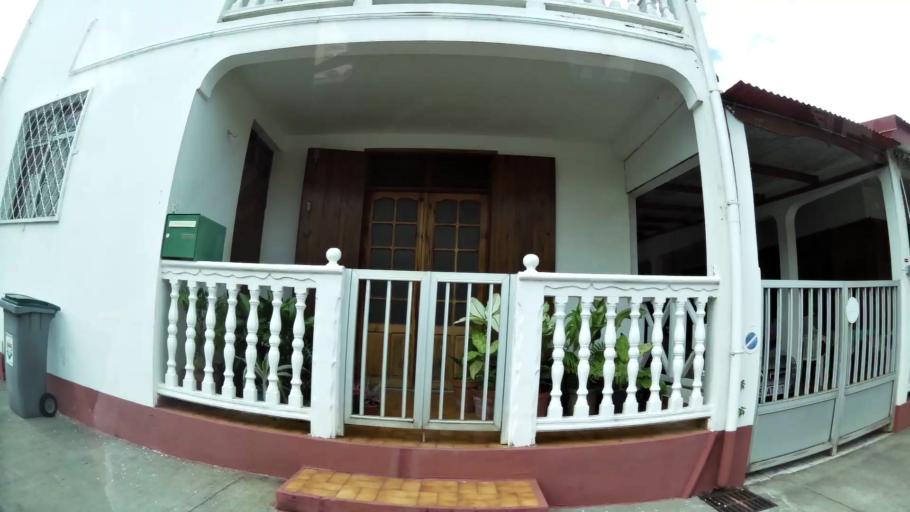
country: GP
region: Guadeloupe
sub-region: Guadeloupe
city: Baie-Mahault
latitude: 16.2667
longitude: -61.5882
